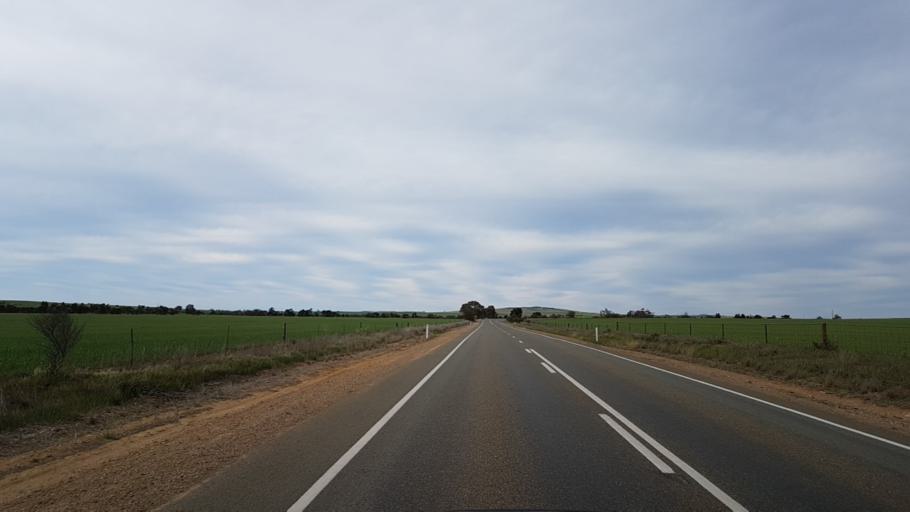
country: AU
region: South Australia
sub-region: Northern Areas
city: Jamestown
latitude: -33.2312
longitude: 138.3928
